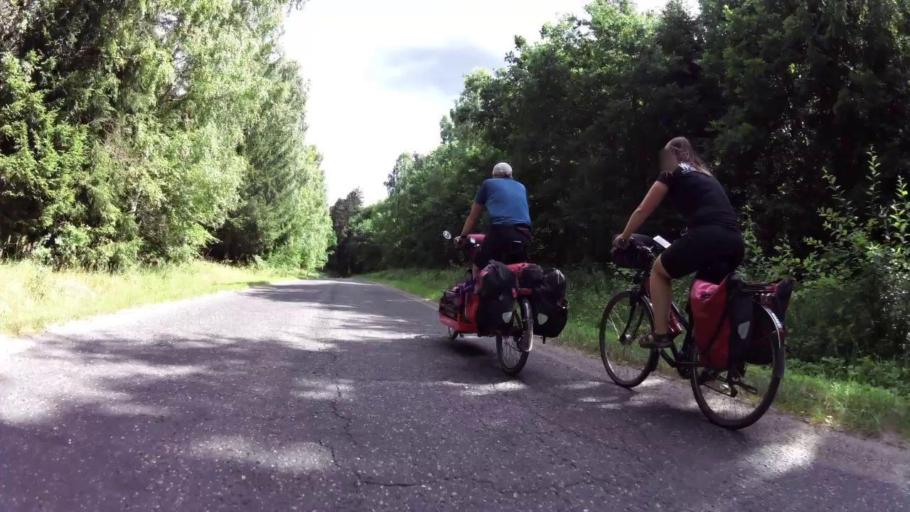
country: PL
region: West Pomeranian Voivodeship
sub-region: Powiat lobeski
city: Lobez
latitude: 53.6619
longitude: 15.5545
